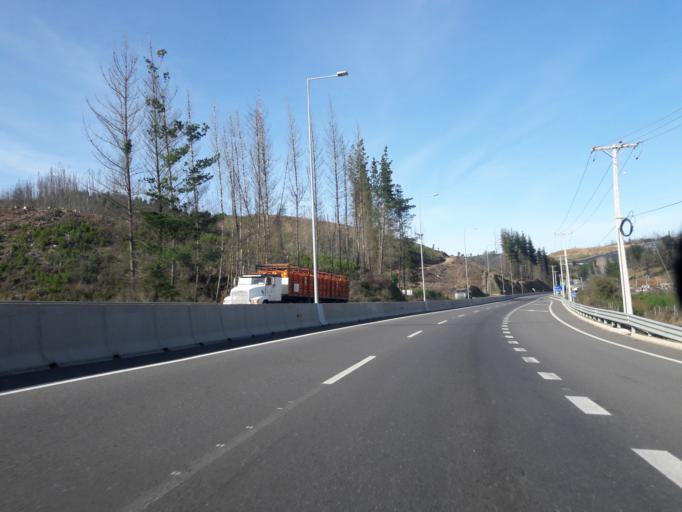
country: CL
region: Biobio
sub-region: Provincia de Concepcion
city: Penco
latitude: -36.8581
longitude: -72.8611
